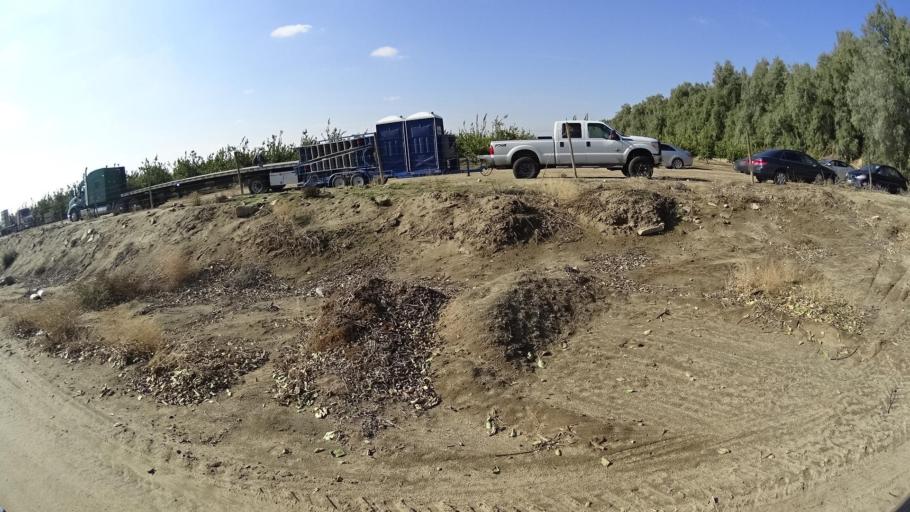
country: US
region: California
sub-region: Kern County
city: Arvin
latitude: 35.2816
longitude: -118.7888
